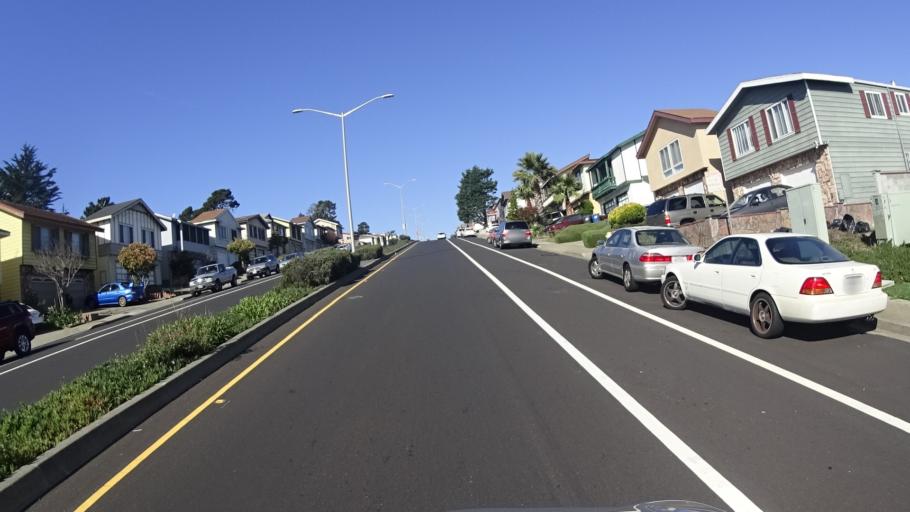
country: US
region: California
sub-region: San Mateo County
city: Colma
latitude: 37.6521
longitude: -122.4582
